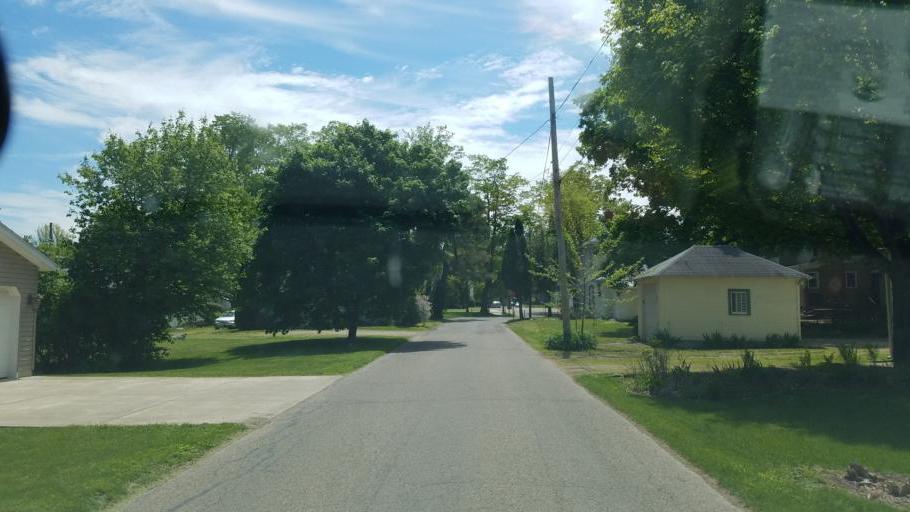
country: US
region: Ohio
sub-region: Knox County
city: Mount Vernon
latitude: 40.3936
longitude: -82.4707
